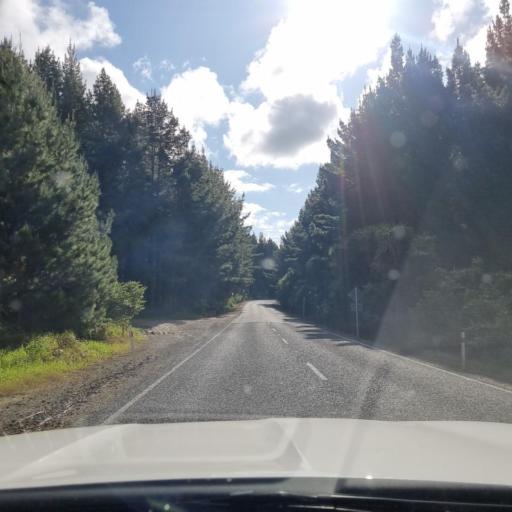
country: NZ
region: Northland
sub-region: Kaipara District
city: Dargaville
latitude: -36.2357
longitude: 174.0458
